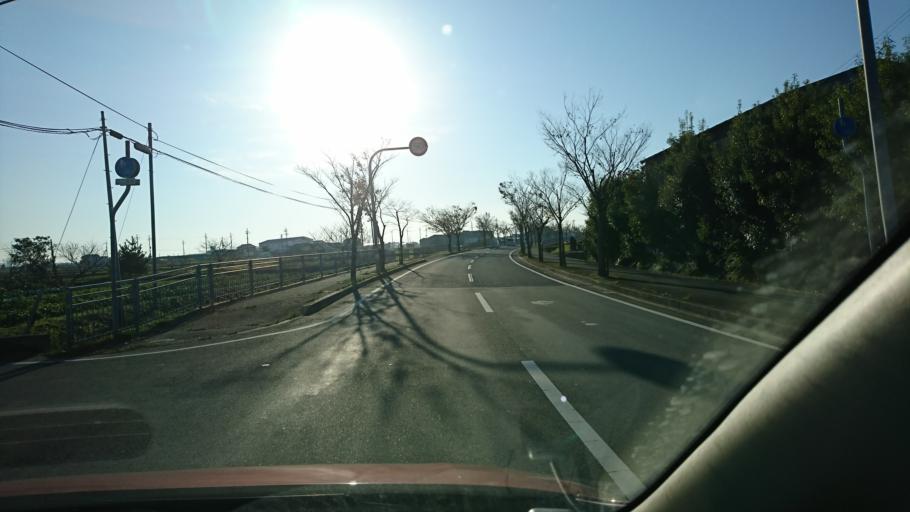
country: JP
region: Hyogo
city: Miki
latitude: 34.7708
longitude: 134.9104
